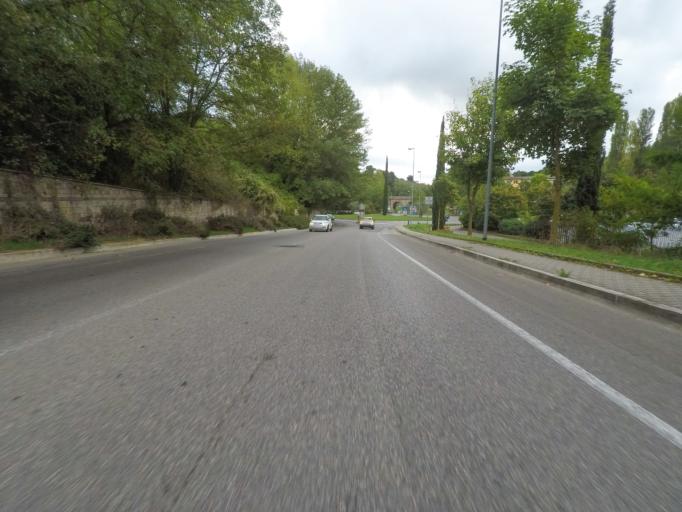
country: IT
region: Tuscany
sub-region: Provincia di Siena
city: Siena
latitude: 43.3280
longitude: 11.3369
